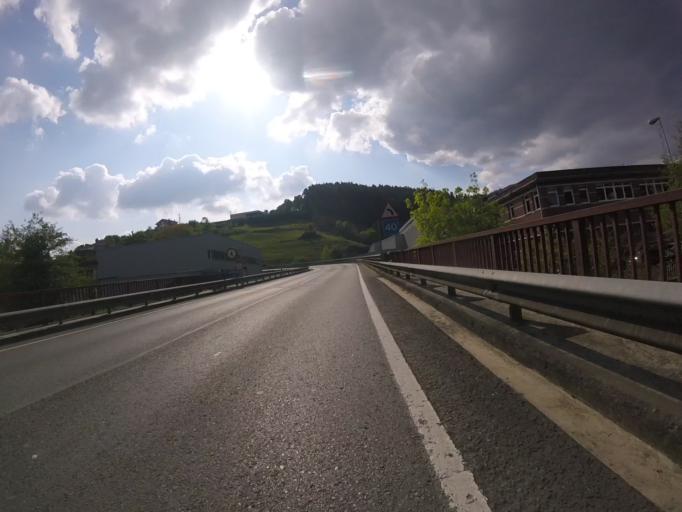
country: ES
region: Basque Country
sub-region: Provincia de Guipuzcoa
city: Azkoitia
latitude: 43.1737
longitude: -2.3198
